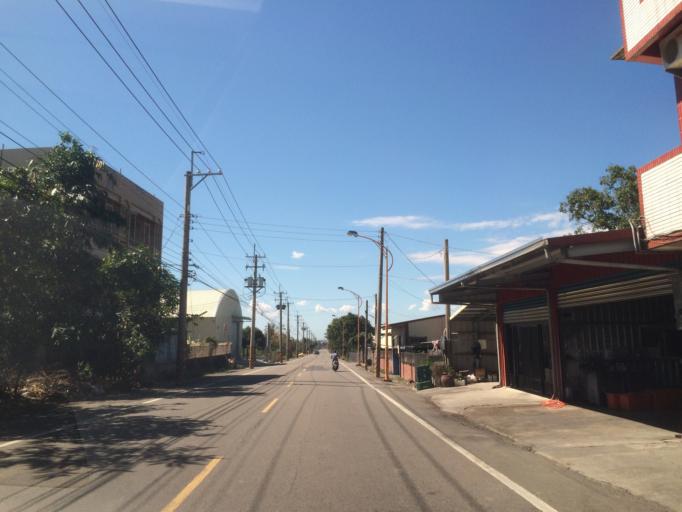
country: TW
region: Taiwan
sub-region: Yunlin
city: Douliu
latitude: 23.7032
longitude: 120.5928
